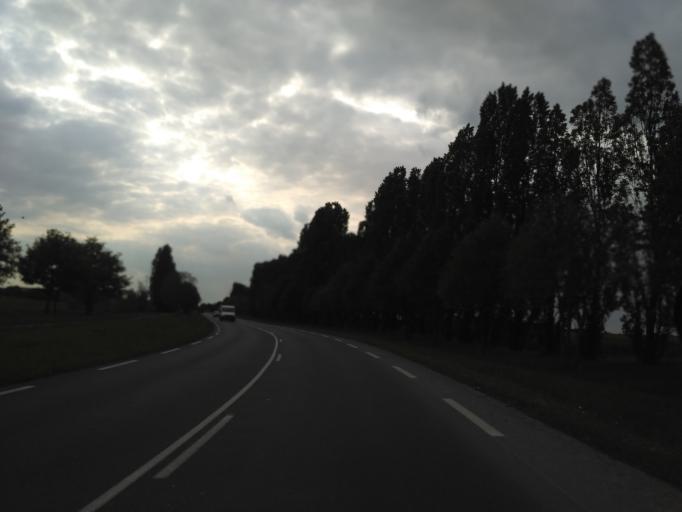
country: FR
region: Ile-de-France
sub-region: Departement de Seine-et-Marne
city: Voisenon
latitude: 48.5746
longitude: 2.6503
